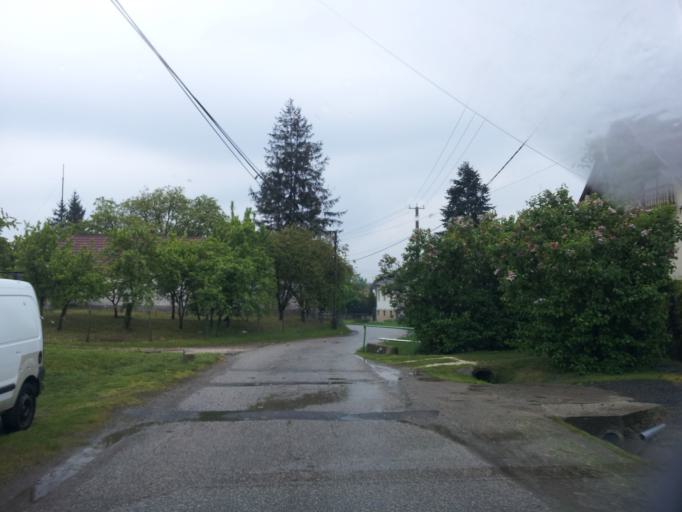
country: HU
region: Baranya
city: Hosszuheteny
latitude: 46.1709
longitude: 18.3489
